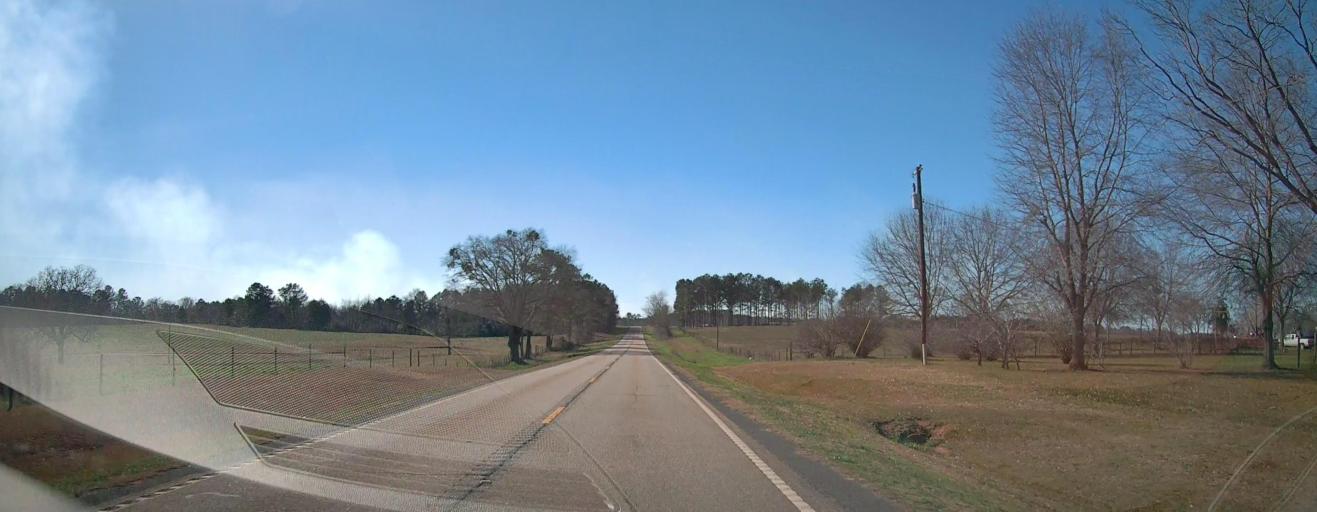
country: US
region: Georgia
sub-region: Schley County
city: Ellaville
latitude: 32.1892
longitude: -84.1984
